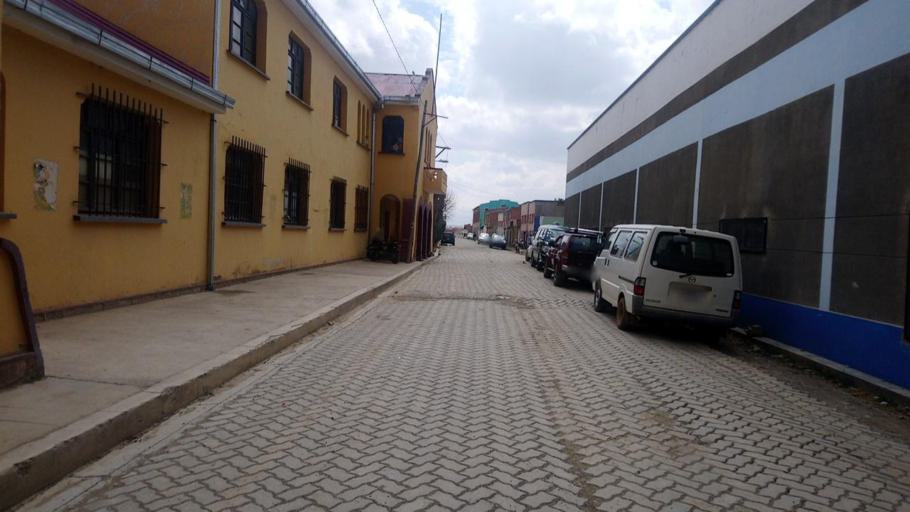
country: BO
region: La Paz
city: Batallas
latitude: -16.3980
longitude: -68.4746
